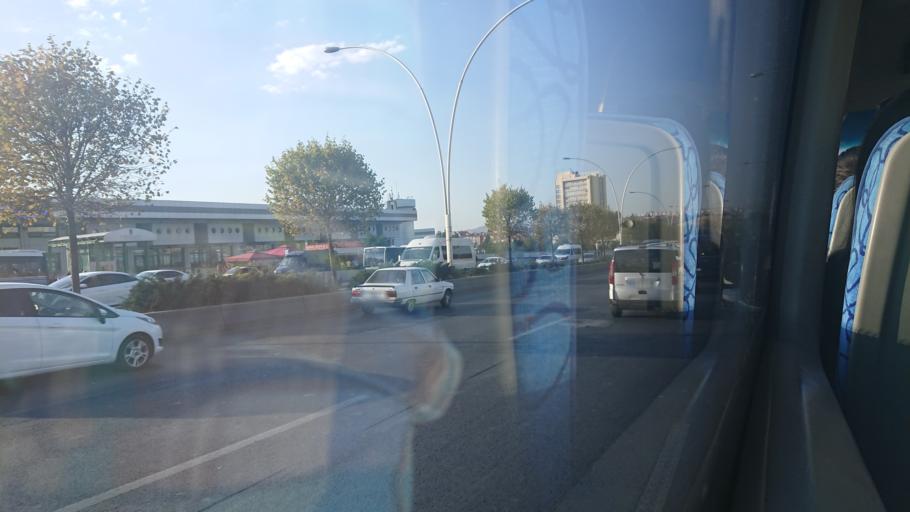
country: TR
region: Ankara
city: Ankara
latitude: 39.9176
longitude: 32.8147
